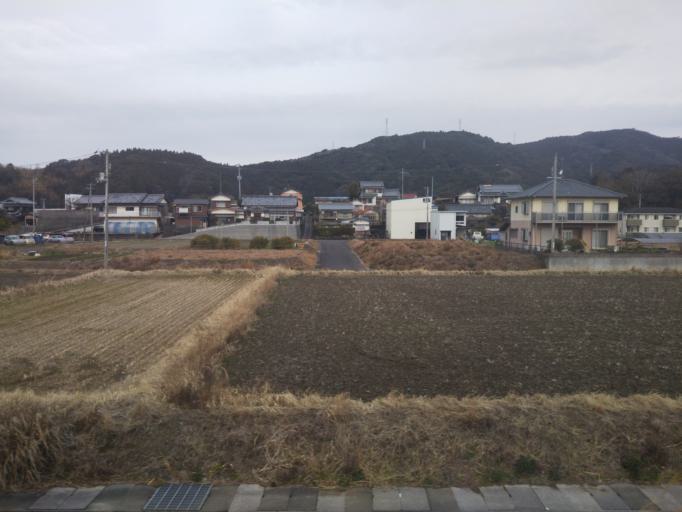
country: JP
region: Kochi
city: Nakamura
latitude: 32.9822
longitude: 132.9568
